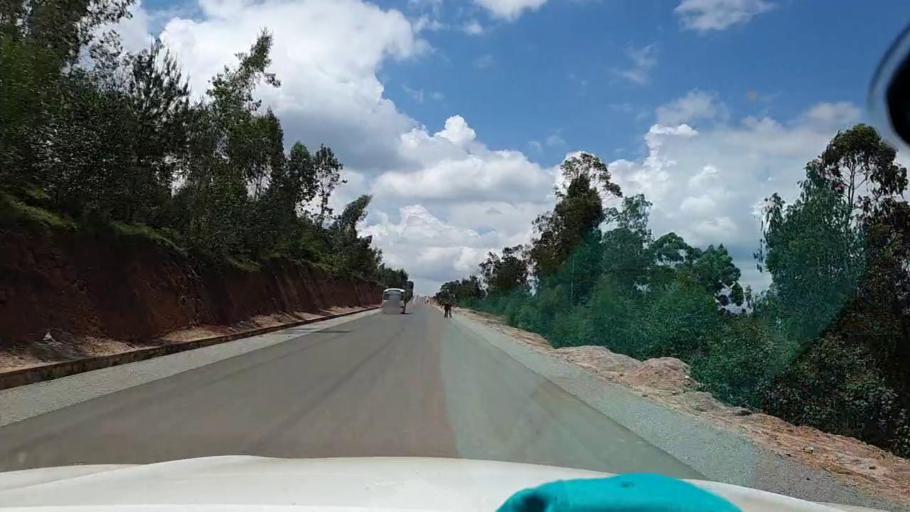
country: RW
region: Southern Province
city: Nzega
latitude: -2.6415
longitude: 29.5771
